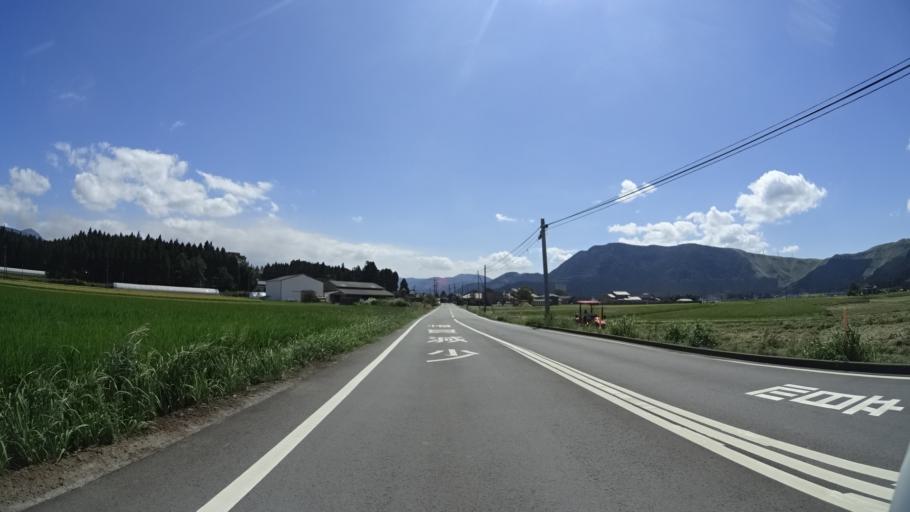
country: JP
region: Kumamoto
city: Aso
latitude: 32.9227
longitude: 130.9941
